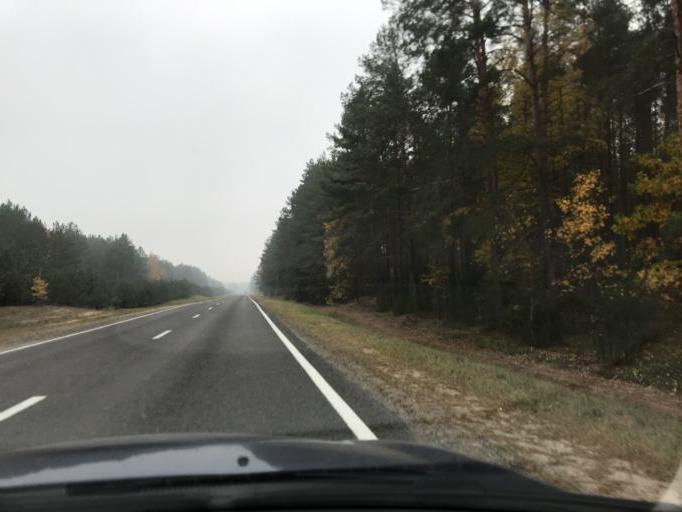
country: LT
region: Alytaus apskritis
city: Druskininkai
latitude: 53.8604
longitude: 23.8928
